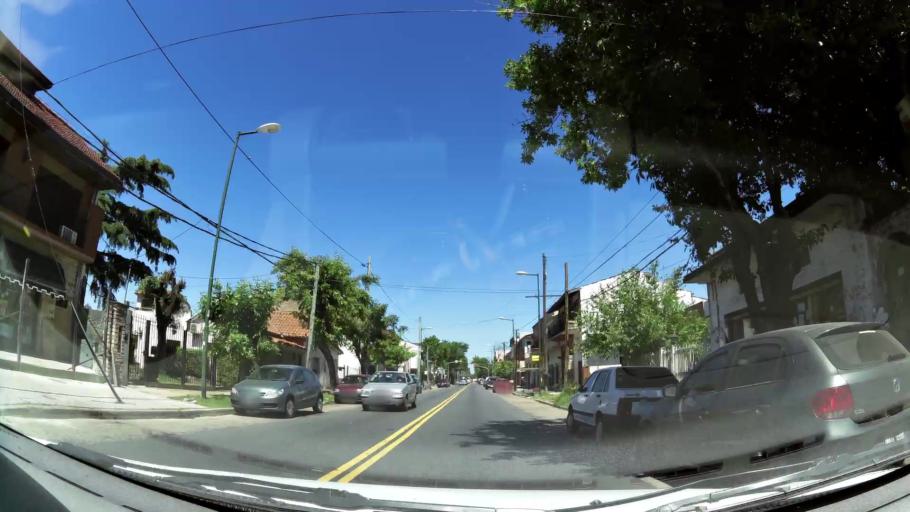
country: AR
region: Buenos Aires
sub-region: Partido de General San Martin
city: General San Martin
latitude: -34.5242
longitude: -58.5543
